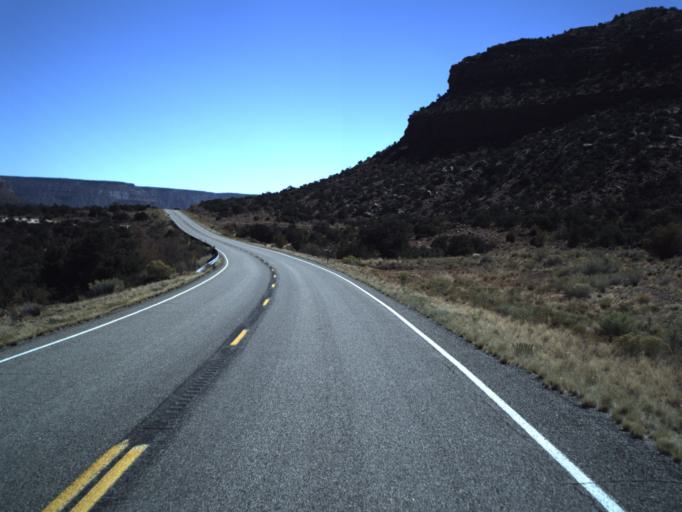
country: US
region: Utah
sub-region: San Juan County
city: Blanding
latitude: 37.6529
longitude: -110.1305
